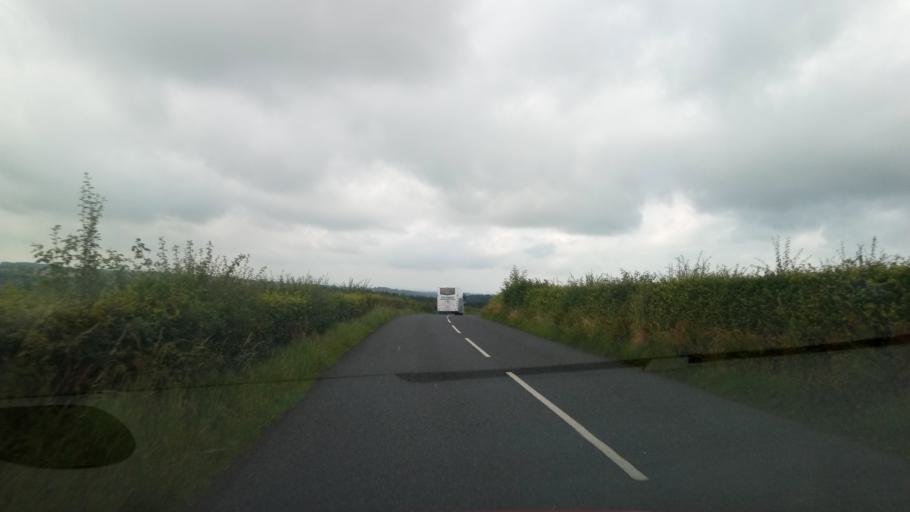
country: GB
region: Scotland
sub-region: Dumfries and Galloway
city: Langholm
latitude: 55.0933
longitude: -2.9019
